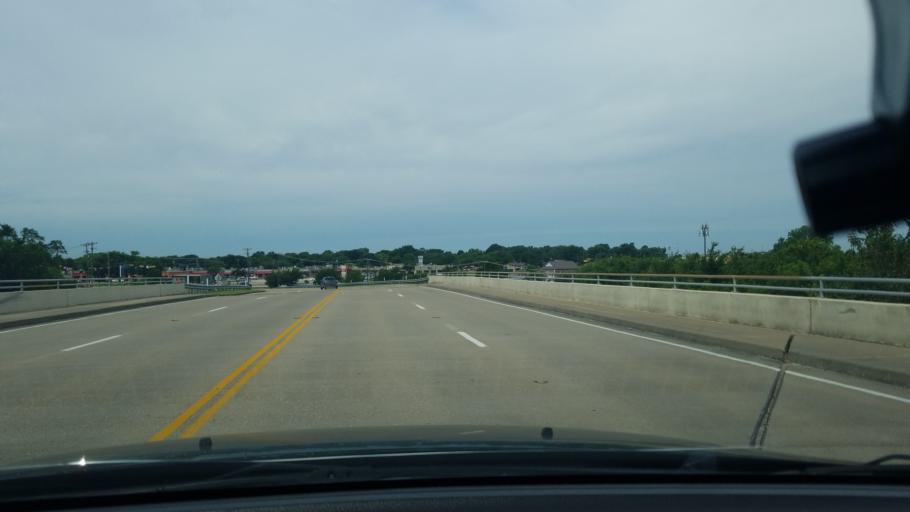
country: US
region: Texas
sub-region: Dallas County
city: Mesquite
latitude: 32.7657
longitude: -96.5803
